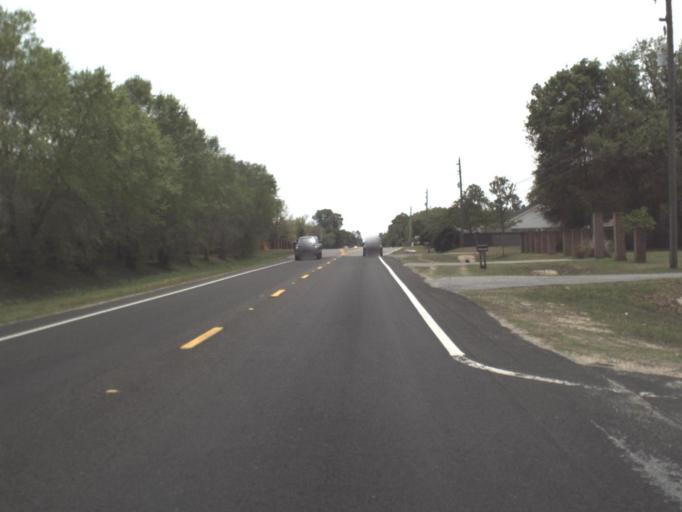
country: US
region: Florida
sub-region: Escambia County
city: Bellview
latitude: 30.4806
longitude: -87.3235
